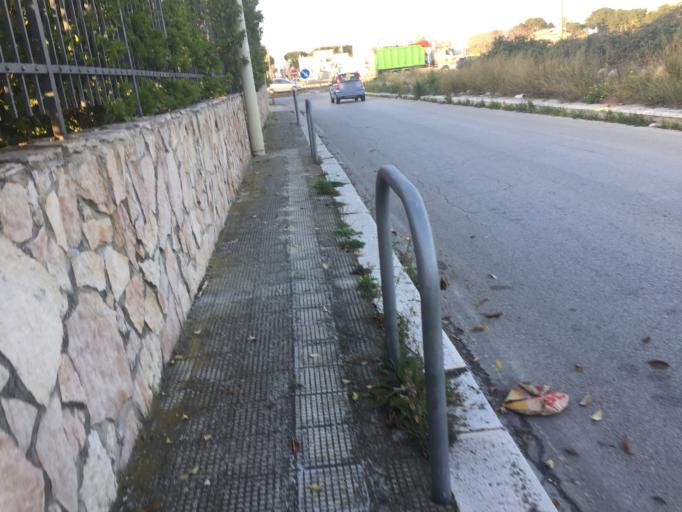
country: IT
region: Apulia
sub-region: Provincia di Bari
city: Parco Scizzo-Parchitello
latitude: 41.0829
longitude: 16.9981
